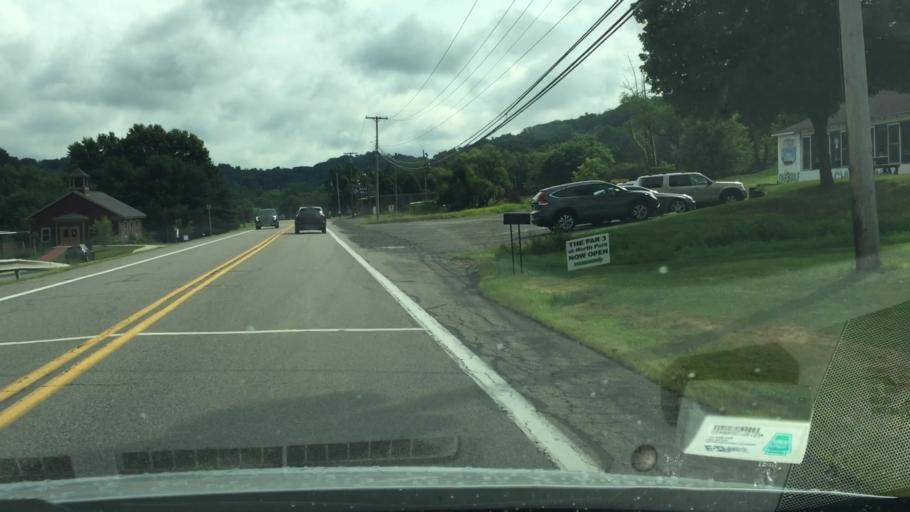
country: US
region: Pennsylvania
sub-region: Allegheny County
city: Gibsonia
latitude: 40.5898
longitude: -80.0187
